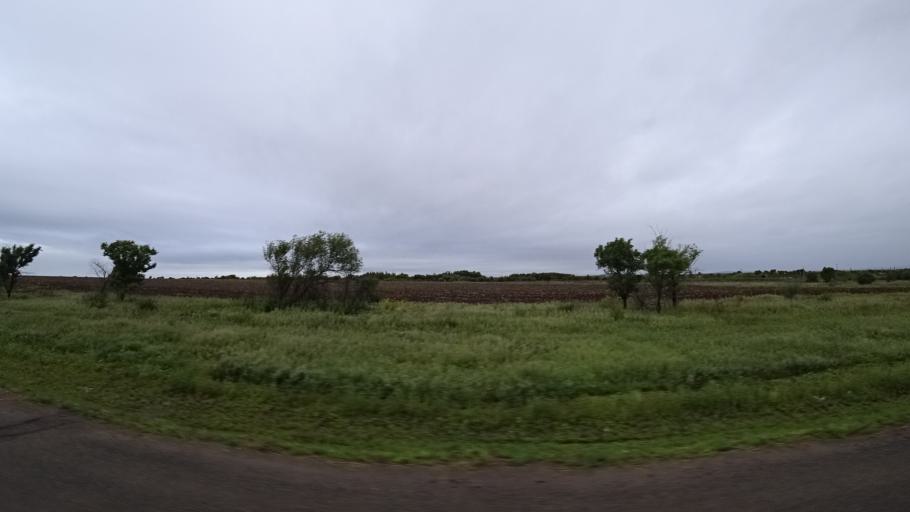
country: RU
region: Primorskiy
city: Chernigovka
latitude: 44.3205
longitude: 132.5676
